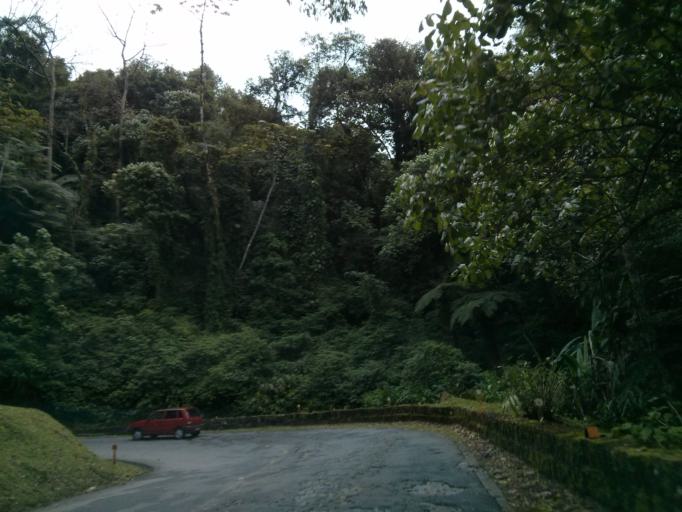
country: BR
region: Parana
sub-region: Campina Grande Do Sul
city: Campina Grande do Sul
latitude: -25.3468
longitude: -48.8863
